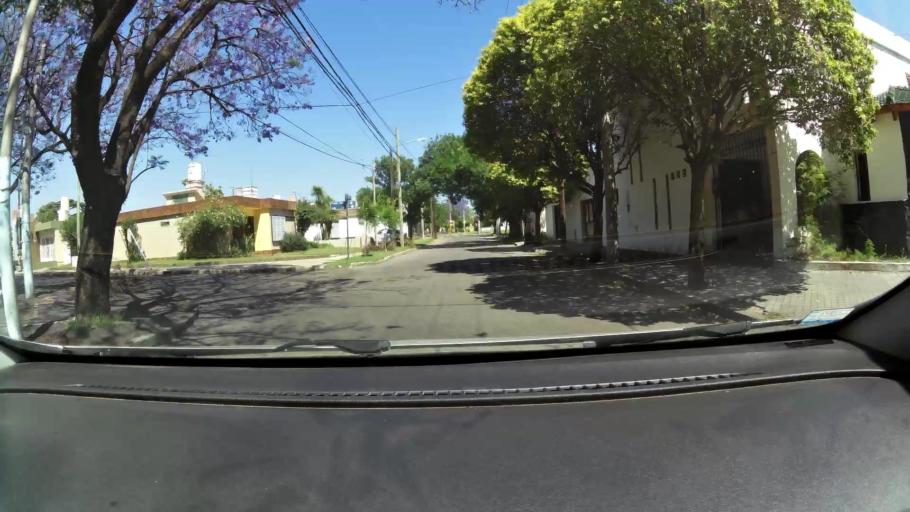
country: AR
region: Cordoba
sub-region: Departamento de Capital
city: Cordoba
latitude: -31.4190
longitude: -64.2156
